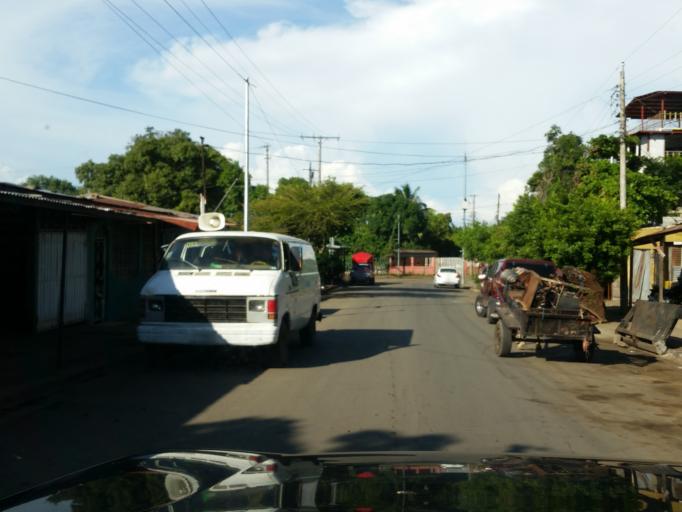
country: NI
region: Managua
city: Managua
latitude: 12.1042
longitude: -86.2209
